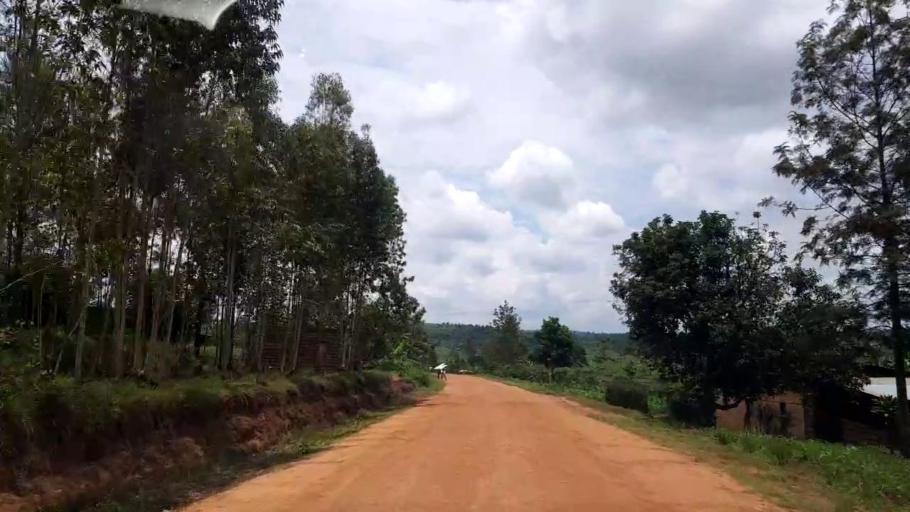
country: RW
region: Northern Province
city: Byumba
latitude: -1.5699
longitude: 30.3010
